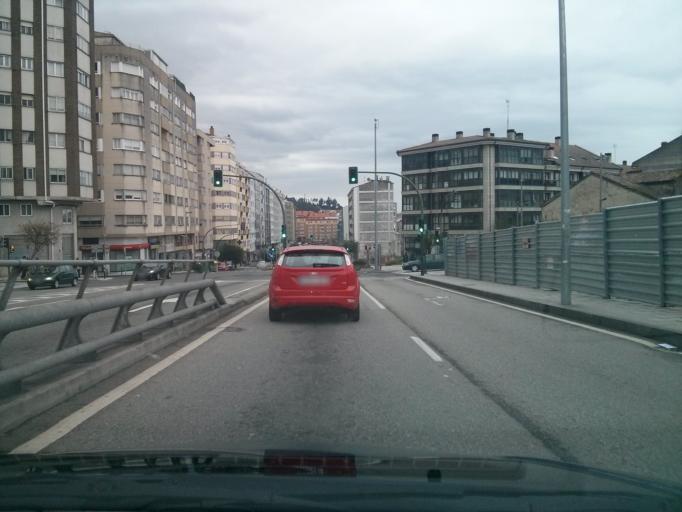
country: ES
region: Galicia
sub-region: Provincia da Coruna
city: Santiago de Compostela
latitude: 42.8724
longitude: -8.5525
